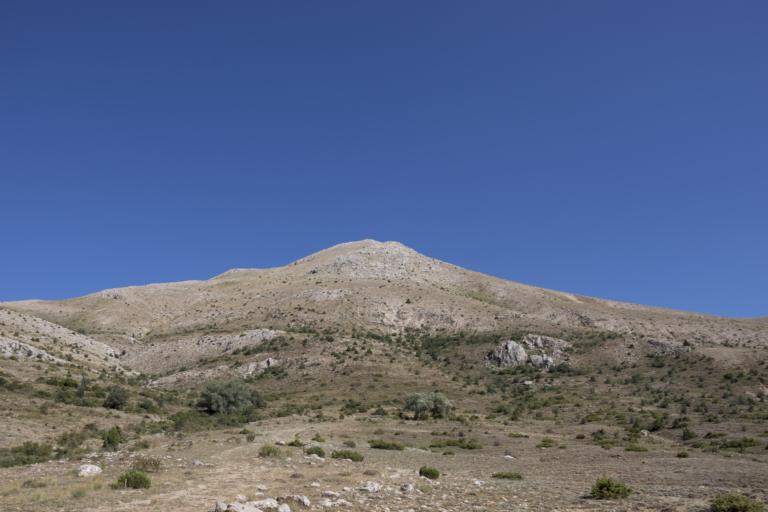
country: TR
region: Kayseri
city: Toklar
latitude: 38.3933
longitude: 36.0938
